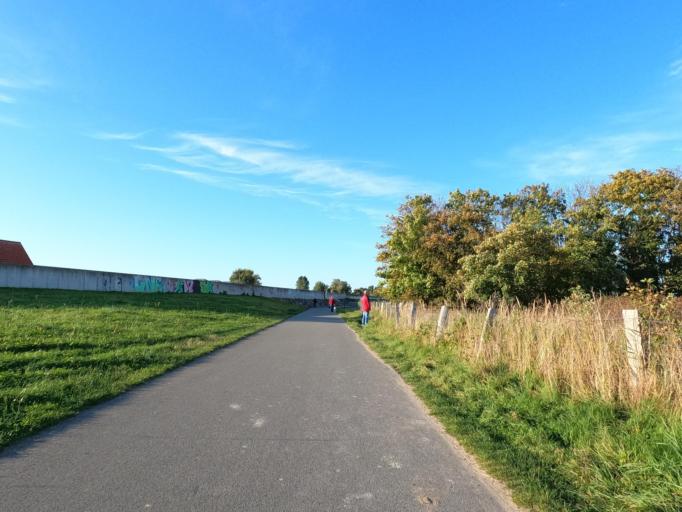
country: DE
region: Schleswig-Holstein
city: Dahme
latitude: 54.2334
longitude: 11.0840
